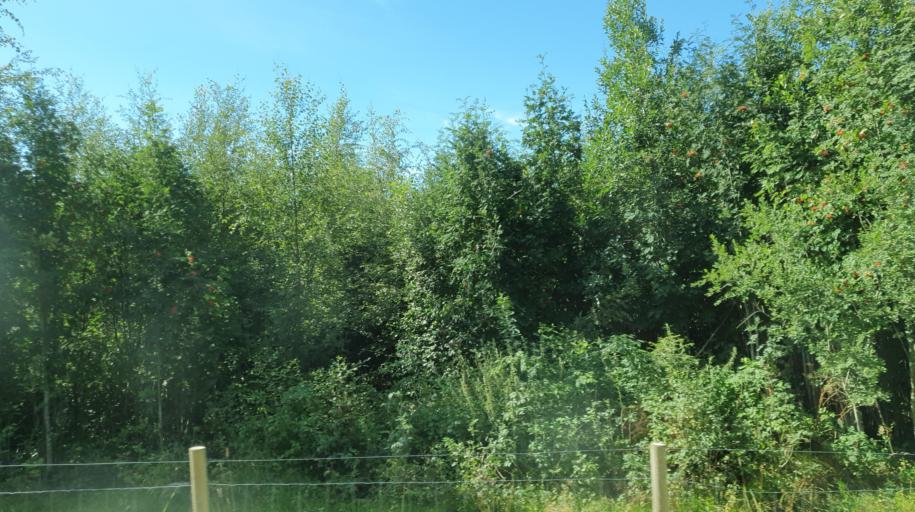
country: NO
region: Nord-Trondelag
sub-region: Levanger
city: Skogn
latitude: 63.6902
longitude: 11.2322
